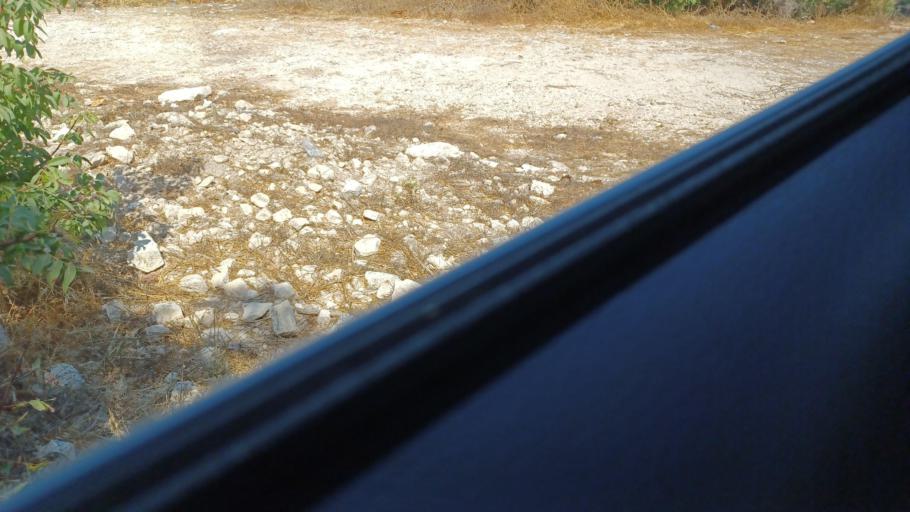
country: CY
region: Pafos
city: Tala
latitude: 34.8600
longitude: 32.4305
